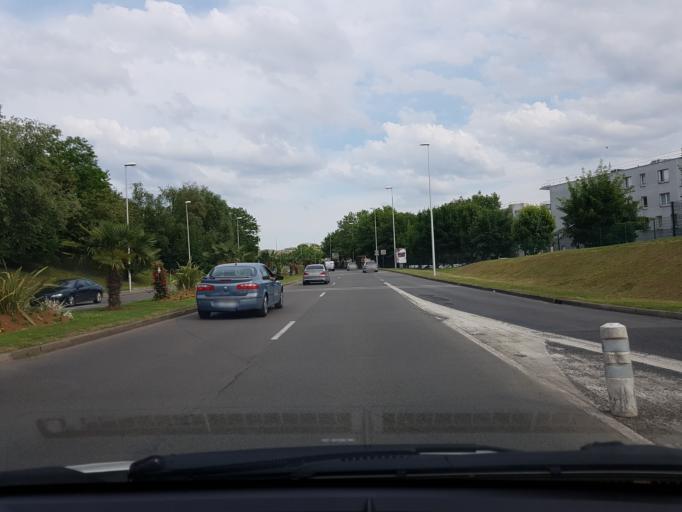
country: FR
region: Ile-de-France
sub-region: Departement de Seine-et-Marne
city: Torcy
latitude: 48.8454
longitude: 2.6474
